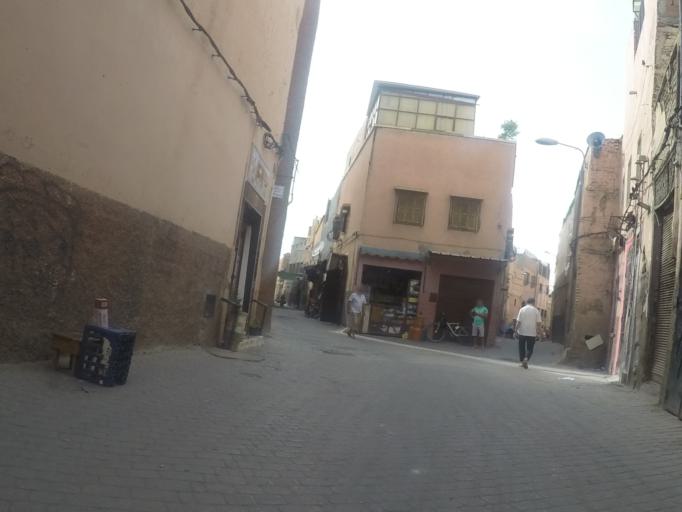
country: MA
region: Marrakech-Tensift-Al Haouz
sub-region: Marrakech
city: Marrakesh
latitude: 31.6290
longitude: -7.9816
